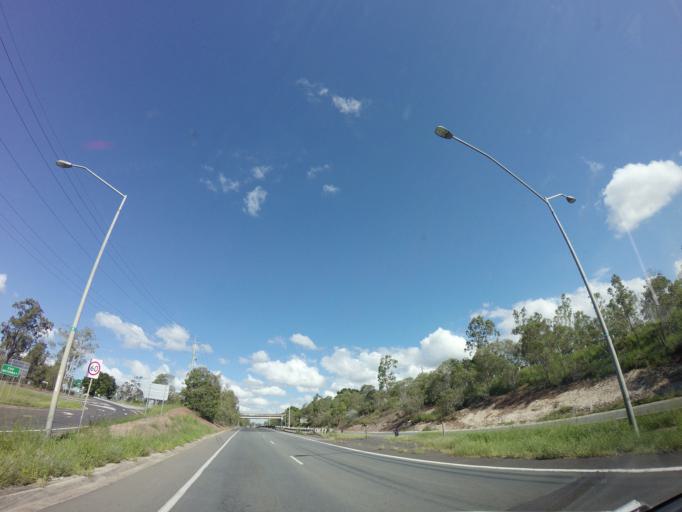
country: AU
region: Queensland
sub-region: Ipswich
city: Riverview
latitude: -27.5905
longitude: 152.8313
